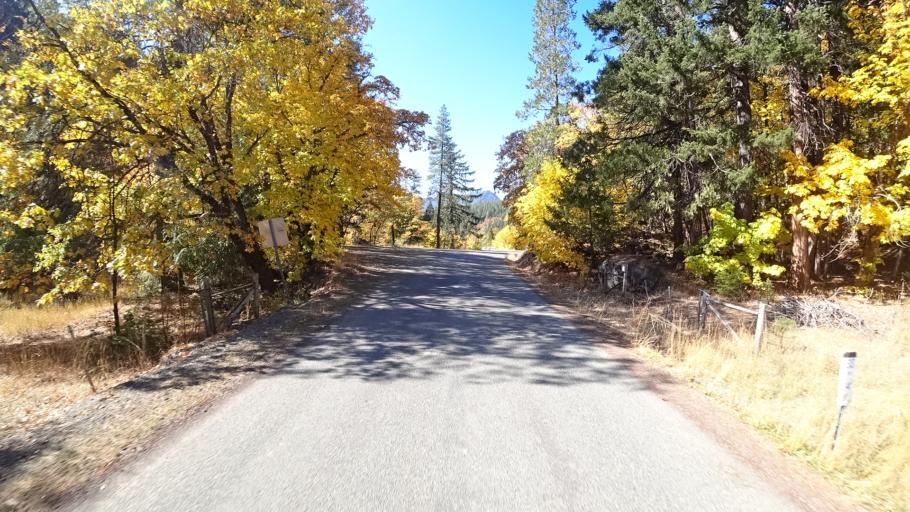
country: US
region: California
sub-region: Siskiyou County
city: Happy Camp
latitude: 41.6357
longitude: -123.0738
